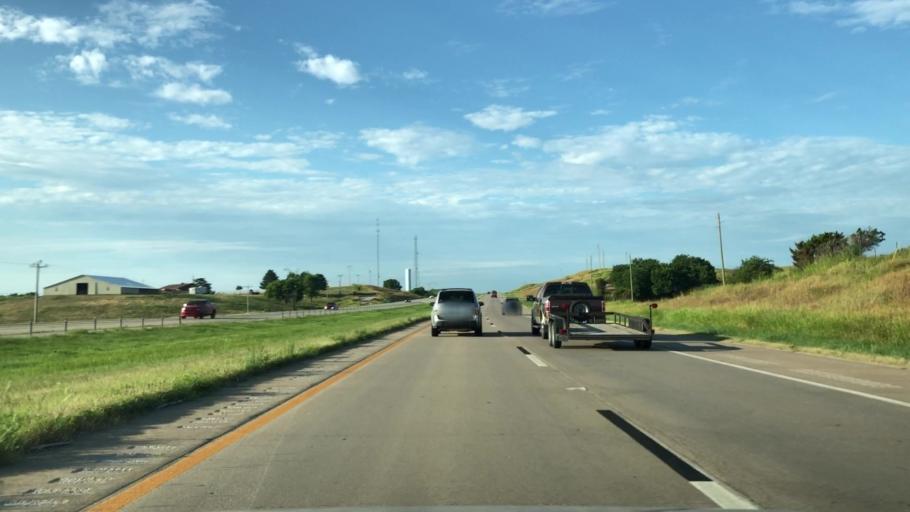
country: US
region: Oklahoma
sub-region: Osage County
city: Skiatook
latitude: 36.5067
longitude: -95.9207
